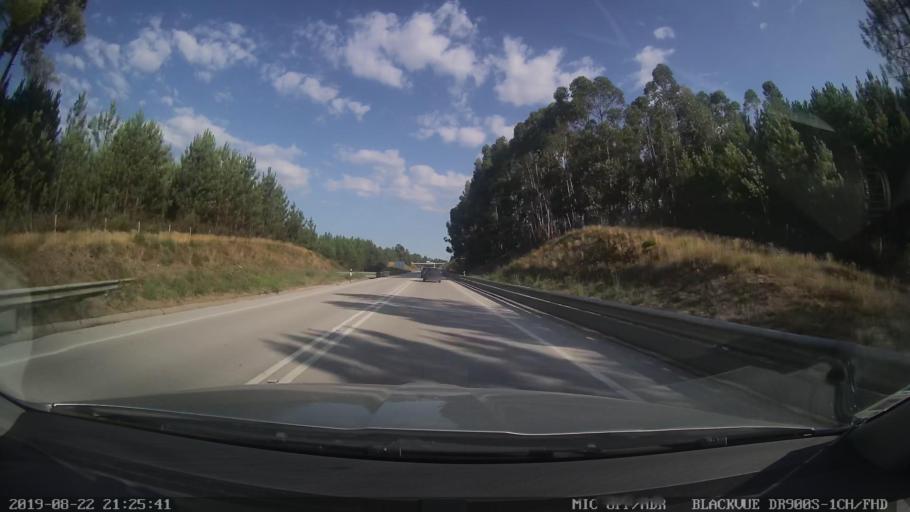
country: PT
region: Castelo Branco
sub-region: Serta
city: Serta
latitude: 39.8574
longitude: -8.1261
